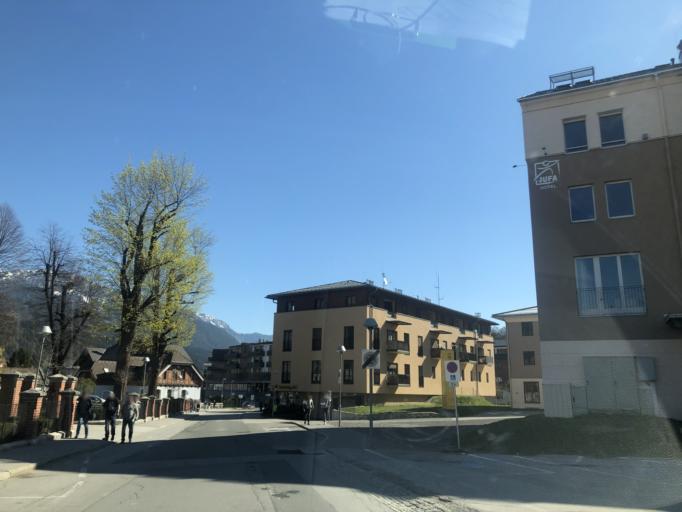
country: AT
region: Styria
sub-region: Politischer Bezirk Liezen
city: Schladming
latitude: 47.3922
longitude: 13.6905
